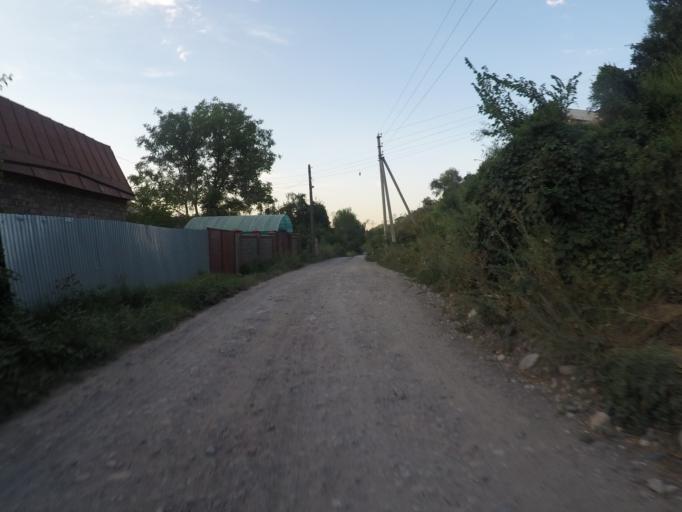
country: KG
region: Chuy
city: Bishkek
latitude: 42.7762
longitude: 74.6437
